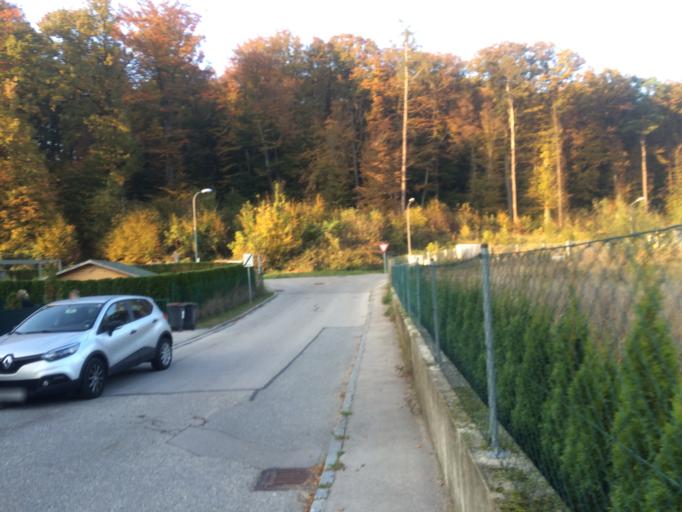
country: AT
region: Lower Austria
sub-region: Politischer Bezirk Wien-Umgebung
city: Gablitz
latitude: 48.2229
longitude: 16.1371
